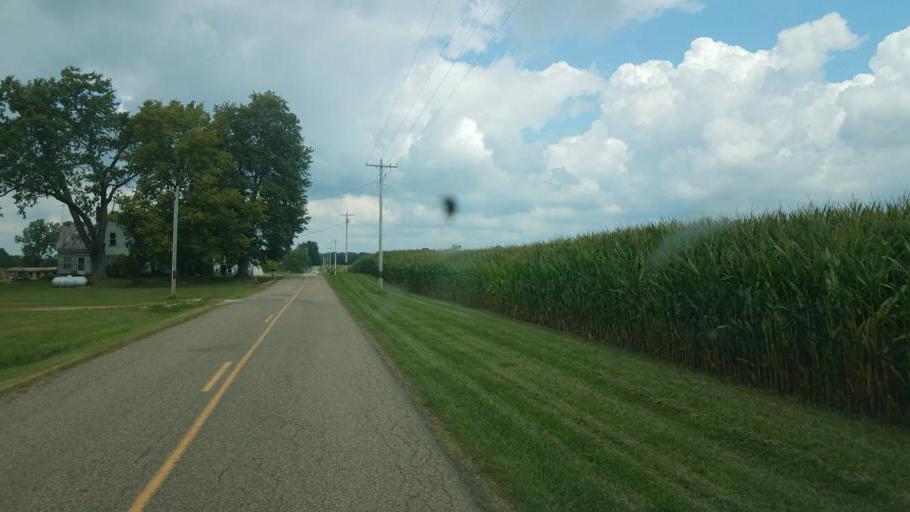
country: US
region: Ohio
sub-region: Licking County
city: Utica
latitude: 40.2915
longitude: -82.4895
